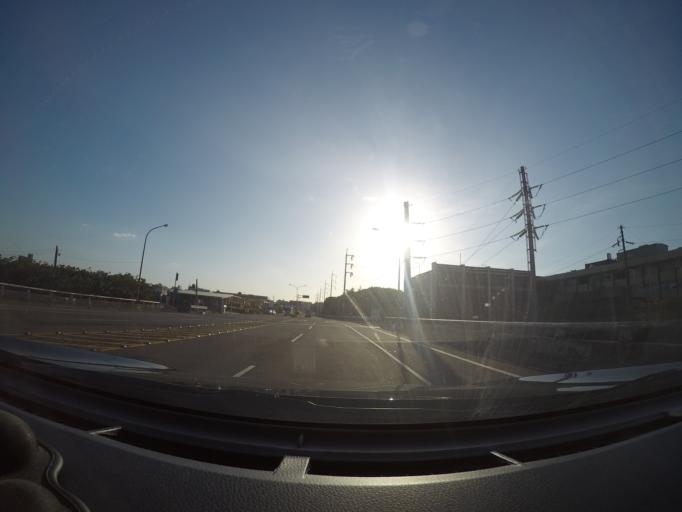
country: TW
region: Taiwan
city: Taoyuan City
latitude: 25.0726
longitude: 121.1989
